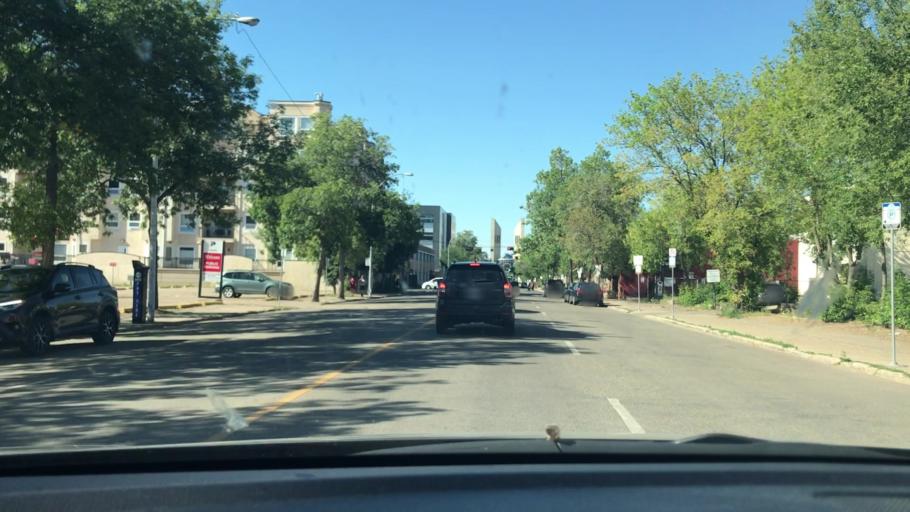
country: CA
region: Alberta
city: Edmonton
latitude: 53.5419
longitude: -113.5048
